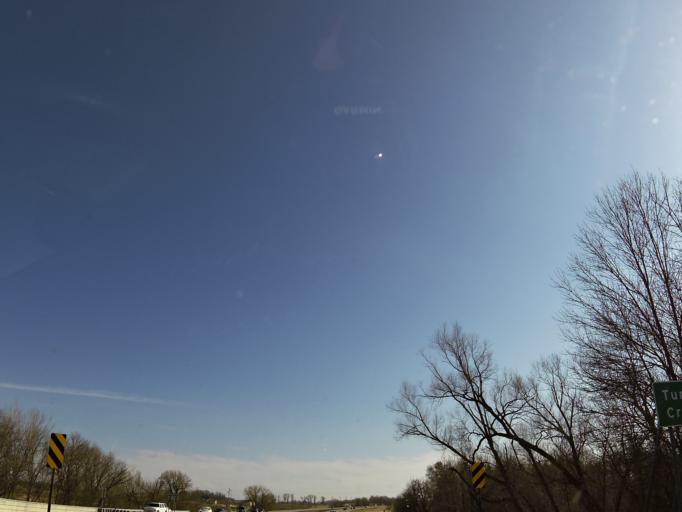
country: US
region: Minnesota
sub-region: Steele County
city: Owatonna
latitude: 44.0332
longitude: -93.2475
